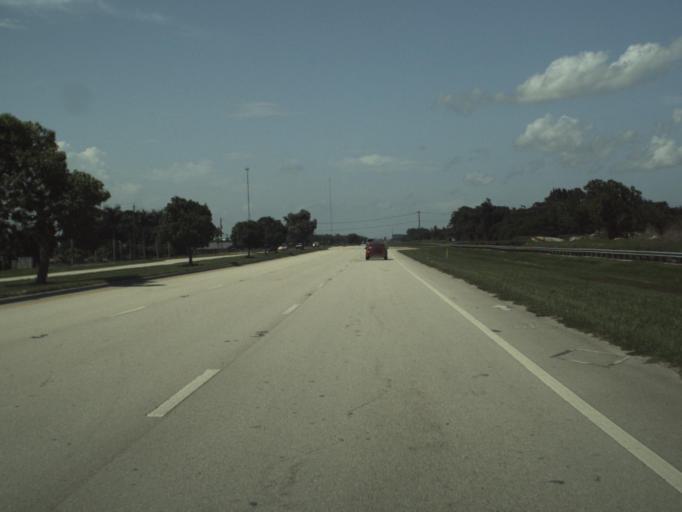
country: US
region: Florida
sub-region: Palm Beach County
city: Villages of Oriole
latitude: 26.5472
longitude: -80.2056
